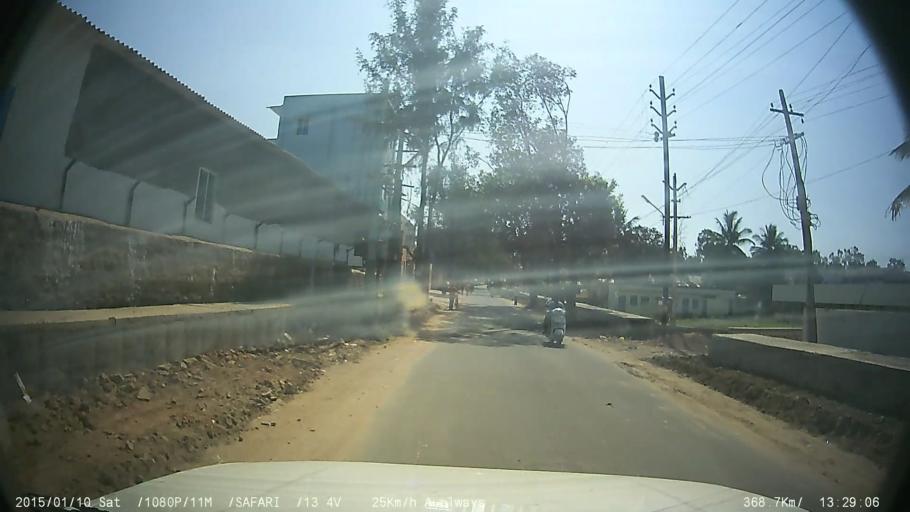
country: IN
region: Tamil Nadu
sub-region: Krishnagiri
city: Hosur
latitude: 12.7708
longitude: 77.7974
